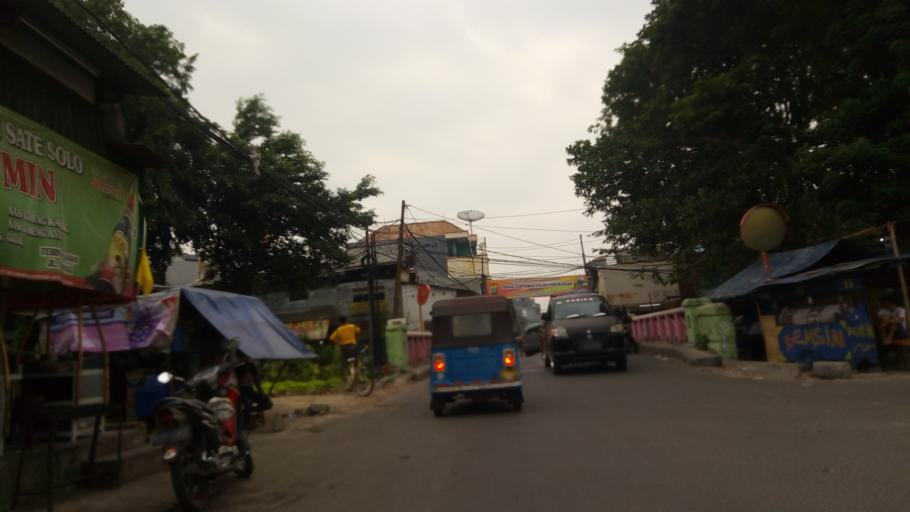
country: ID
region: Jakarta Raya
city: Jakarta
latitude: -6.1423
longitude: 106.8385
